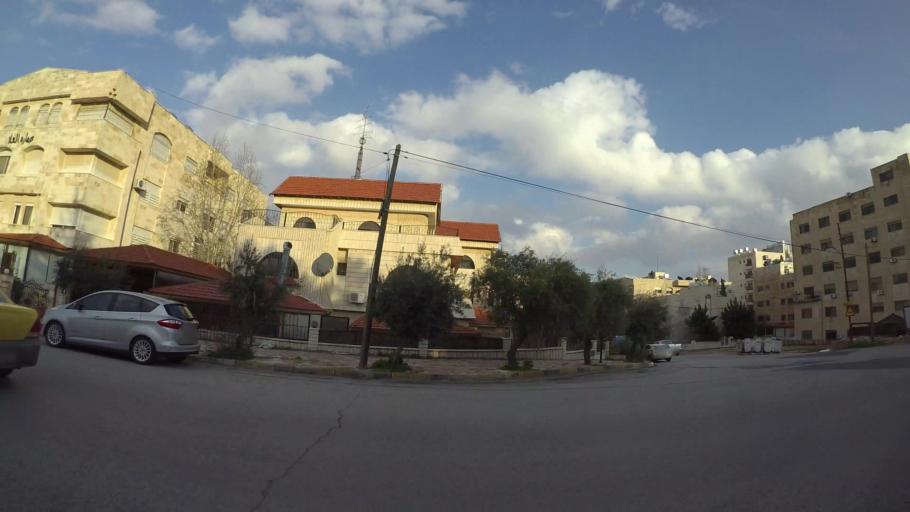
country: JO
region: Amman
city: Al Jubayhah
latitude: 31.9779
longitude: 35.8814
